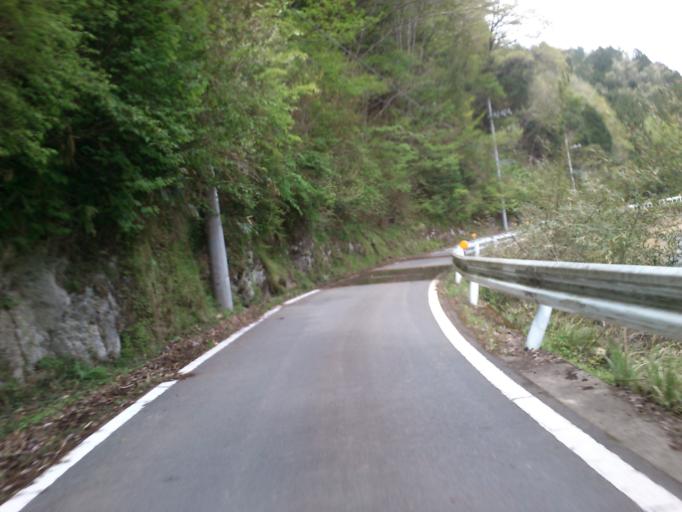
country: JP
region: Kyoto
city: Maizuru
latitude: 35.3963
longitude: 135.4737
